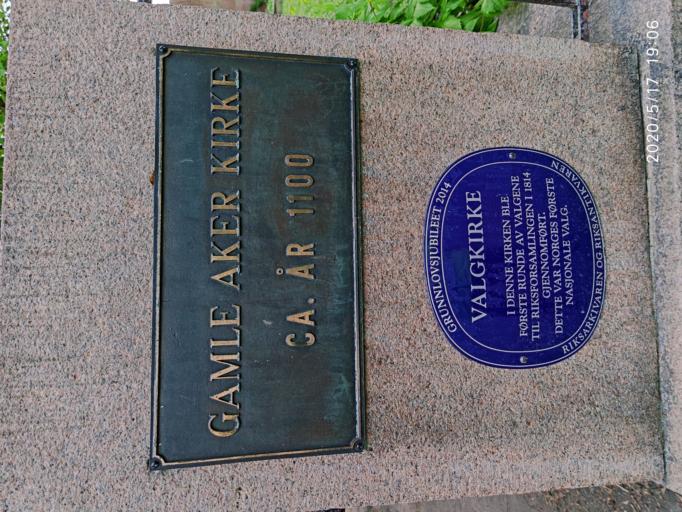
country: NO
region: Oslo
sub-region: Oslo
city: Oslo
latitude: 59.9237
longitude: 10.7465
